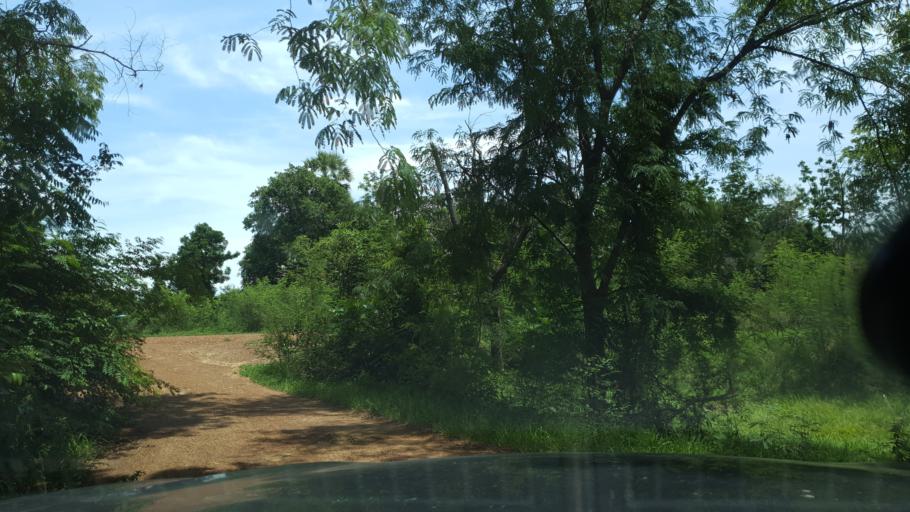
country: TH
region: Sukhothai
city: Ban Na
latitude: 17.0849
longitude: 99.6899
